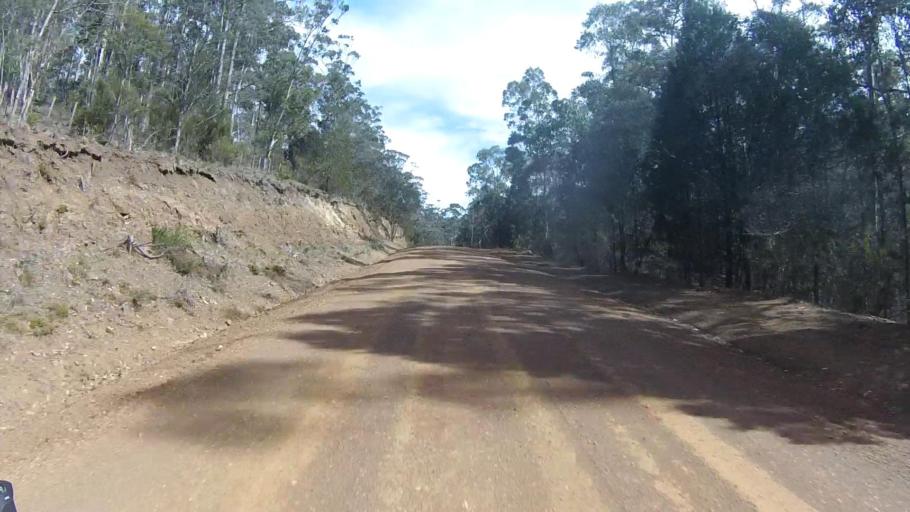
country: AU
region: Tasmania
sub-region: Sorell
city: Sorell
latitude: -42.6151
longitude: 147.8994
